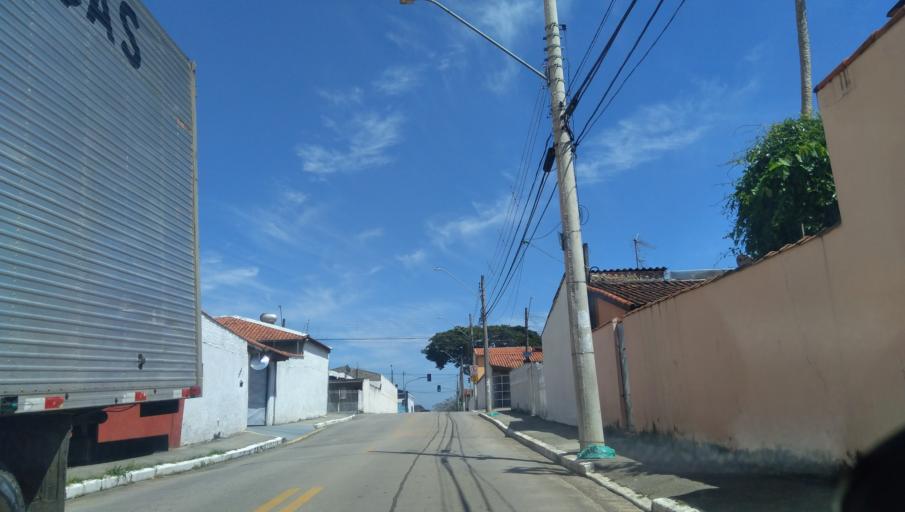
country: BR
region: Sao Paulo
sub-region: Sao Jose Dos Campos
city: Sao Jose dos Campos
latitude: -23.1761
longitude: -45.8490
